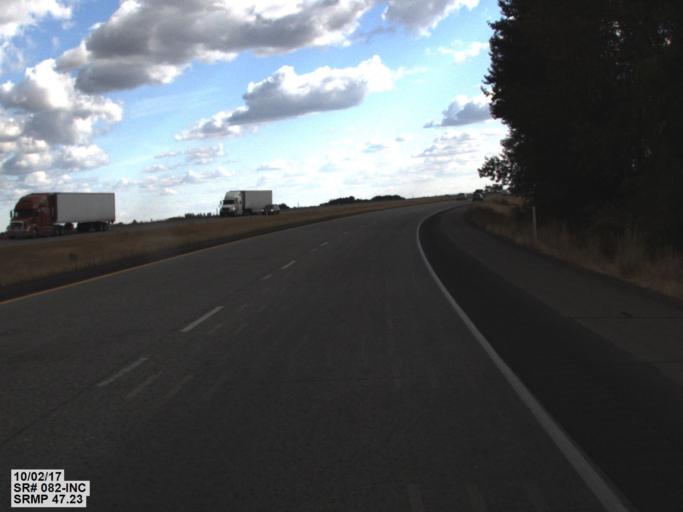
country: US
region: Washington
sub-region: Yakima County
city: Wapato
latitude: 46.4450
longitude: -120.3489
